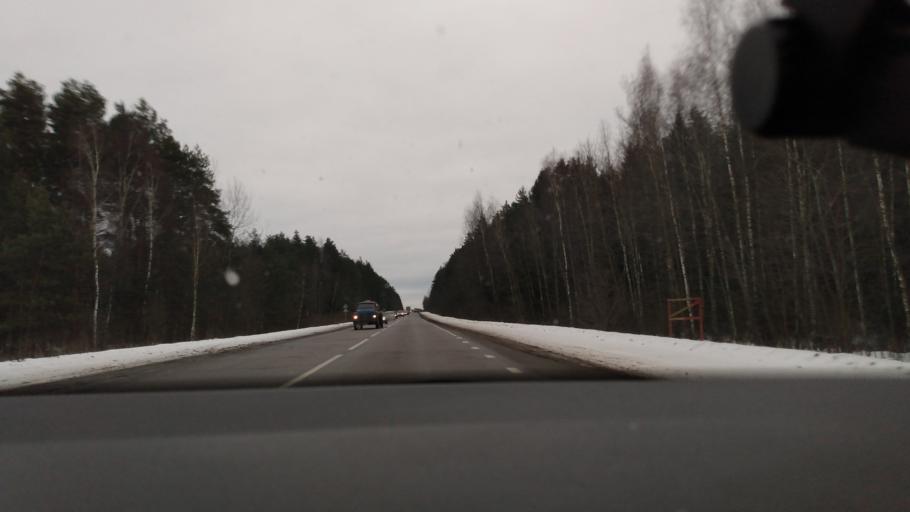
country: RU
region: Moskovskaya
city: Yegor'yevsk
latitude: 55.4324
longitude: 39.0282
